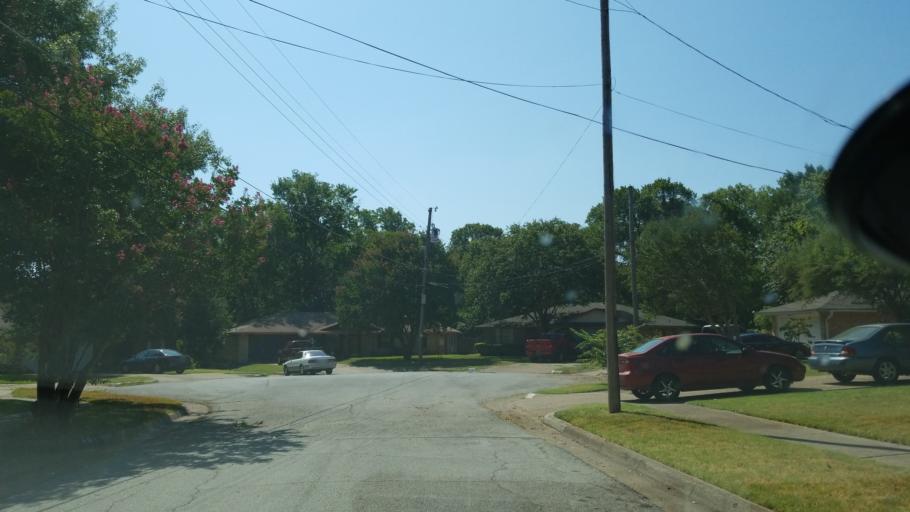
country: US
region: Texas
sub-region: Dallas County
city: Duncanville
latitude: 32.6541
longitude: -96.9010
